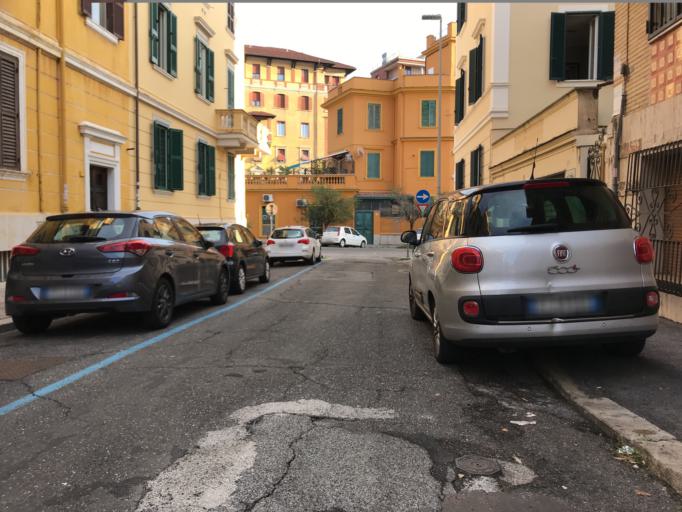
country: IT
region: Latium
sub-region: Citta metropolitana di Roma Capitale
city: Rome
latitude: 41.9102
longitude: 12.5160
